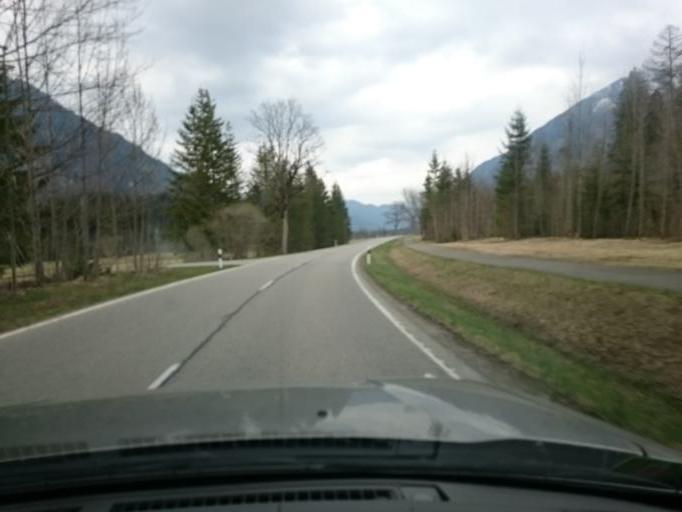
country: DE
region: Bavaria
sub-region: Upper Bavaria
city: Unterammergau
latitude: 47.5699
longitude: 11.0048
